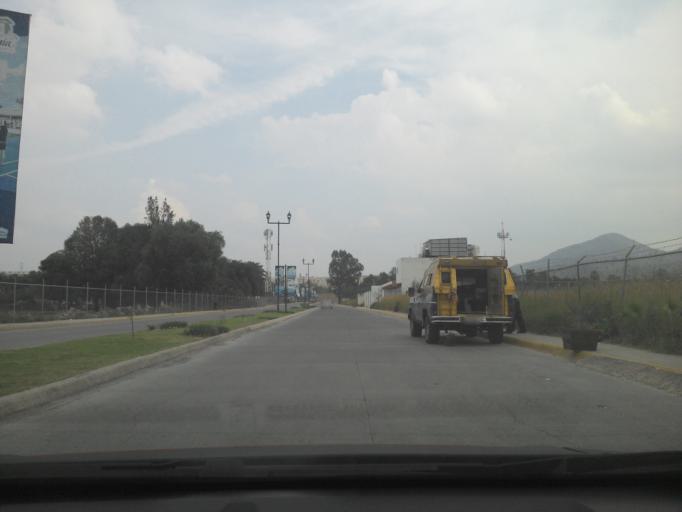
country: MX
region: Jalisco
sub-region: Tlajomulco de Zuniga
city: Lomas de San Agustin
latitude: 20.5301
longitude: -103.4689
